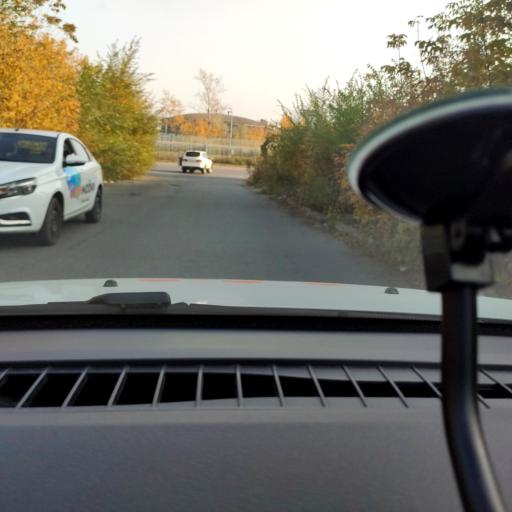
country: RU
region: Samara
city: Petra-Dubrava
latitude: 53.2583
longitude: 50.2851
